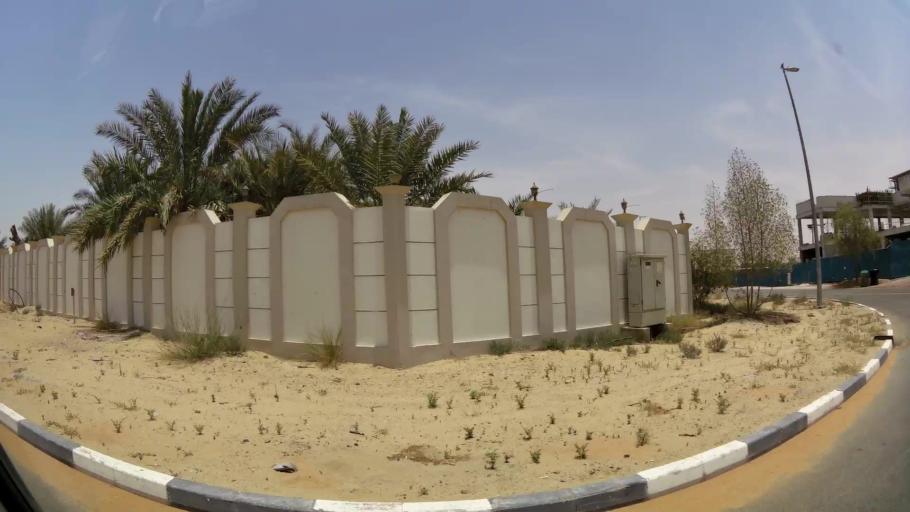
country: AE
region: Ash Shariqah
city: Sharjah
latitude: 25.2316
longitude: 55.4537
